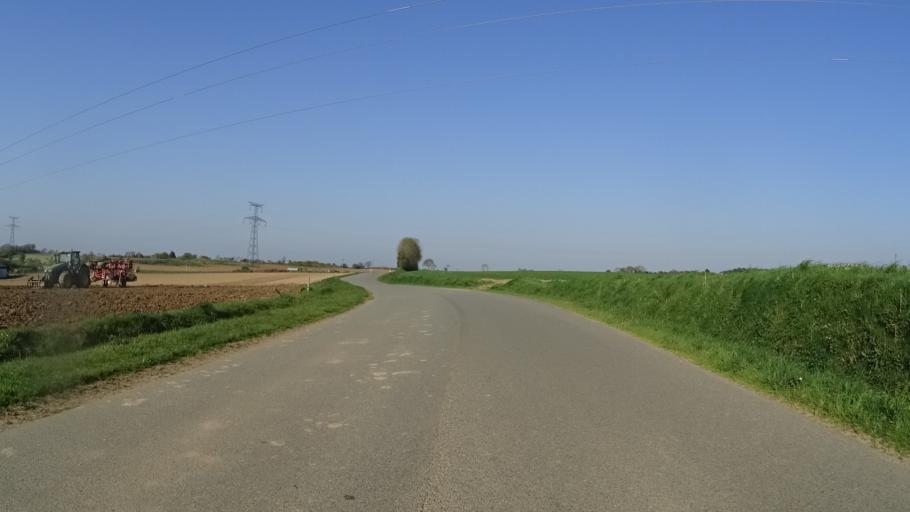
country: FR
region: Brittany
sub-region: Departement du Finistere
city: Irvillac
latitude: 48.3850
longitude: -4.1670
